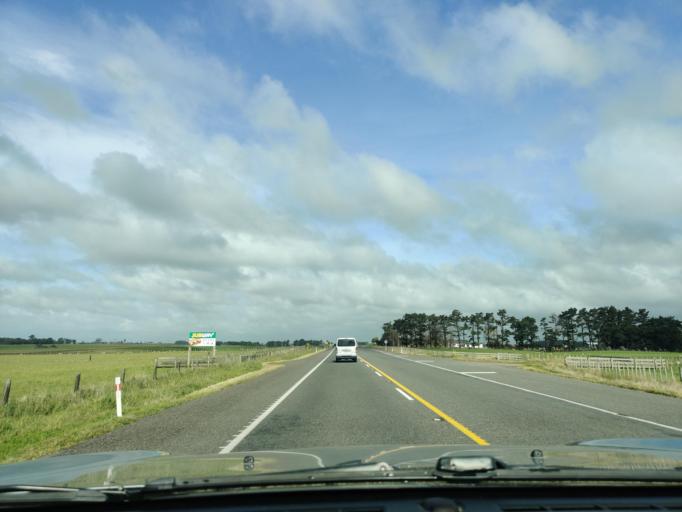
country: NZ
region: Manawatu-Wanganui
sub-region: Rangitikei District
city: Bulls
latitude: -40.0859
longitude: 175.2657
